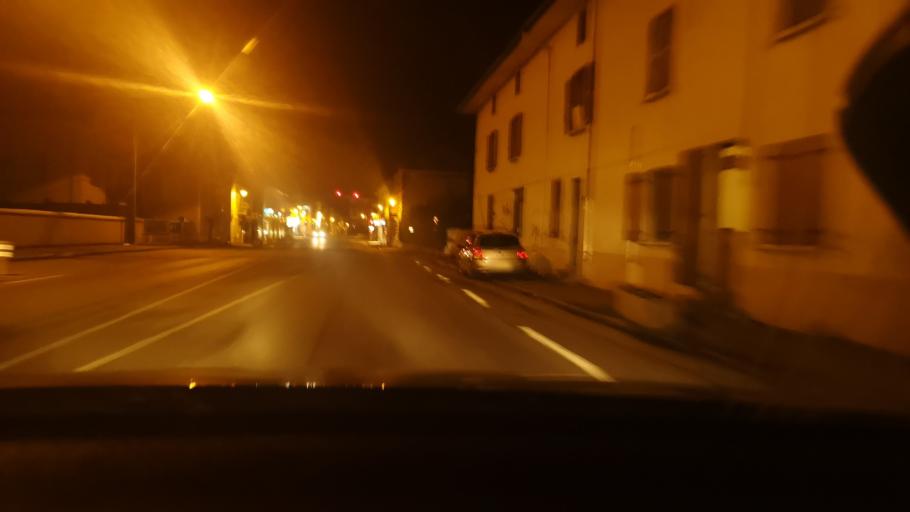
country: FR
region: Rhone-Alpes
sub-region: Departement de l'Ain
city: Montrevel-en-Bresse
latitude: 46.3350
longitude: 5.1298
